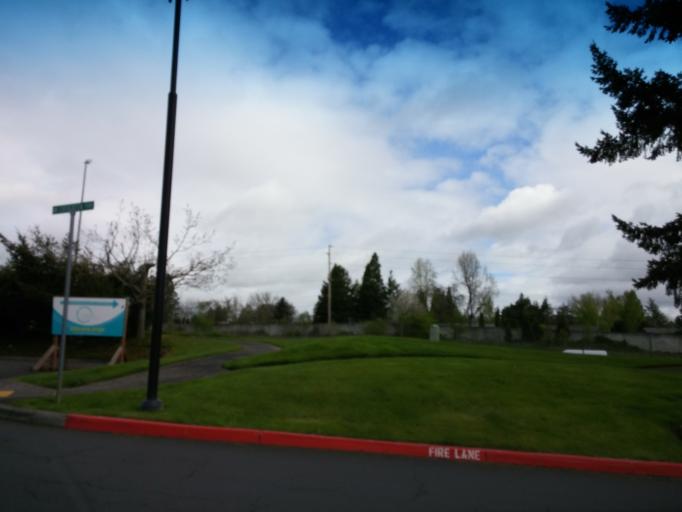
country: US
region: Oregon
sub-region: Washington County
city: Oak Hills
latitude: 45.5381
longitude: -122.8595
